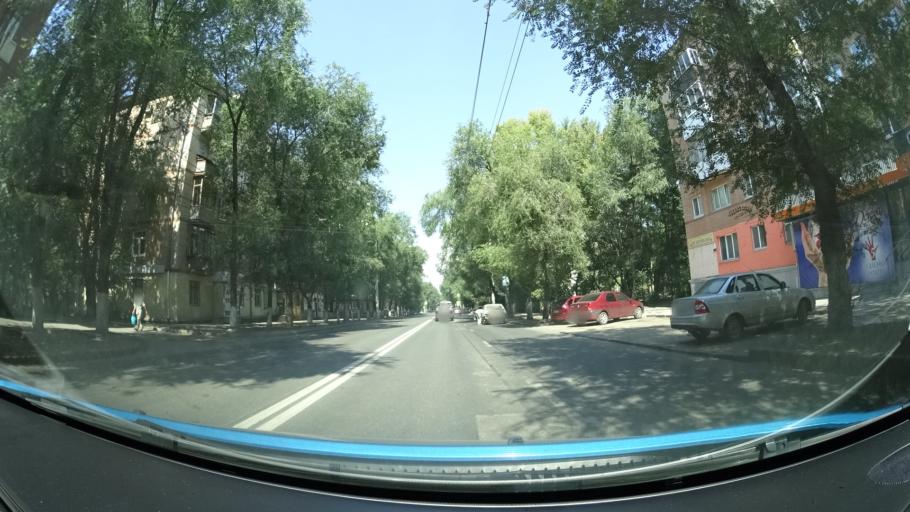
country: RU
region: Samara
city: Samara
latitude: 53.2059
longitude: 50.1624
